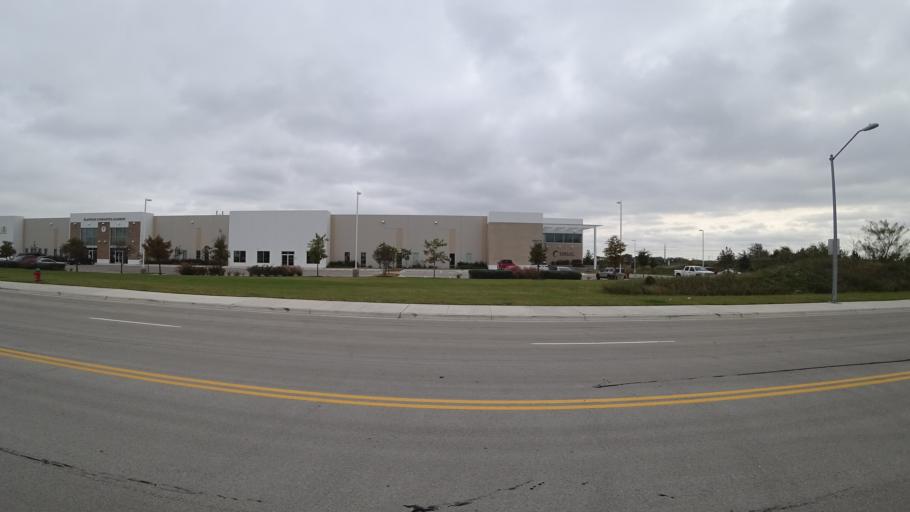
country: US
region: Texas
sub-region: Travis County
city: Pflugerville
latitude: 30.4189
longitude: -97.5908
